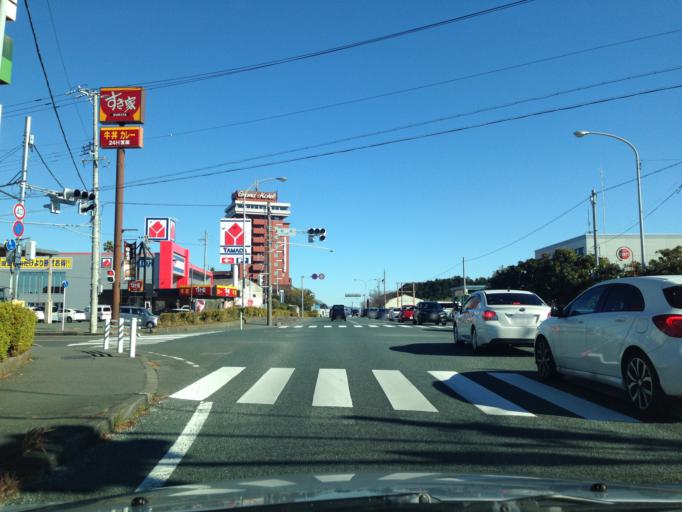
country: JP
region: Shizuoka
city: Fukuroi
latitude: 34.7342
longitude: 137.8775
